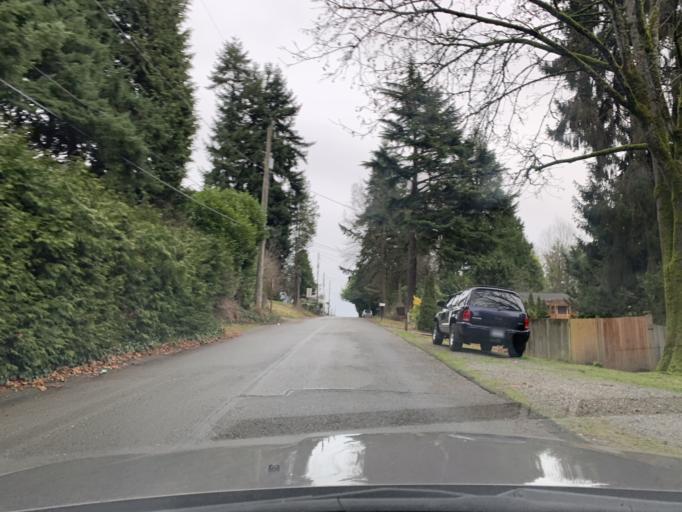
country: US
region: Washington
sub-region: King County
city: Tukwila
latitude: 47.4687
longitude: -122.2757
